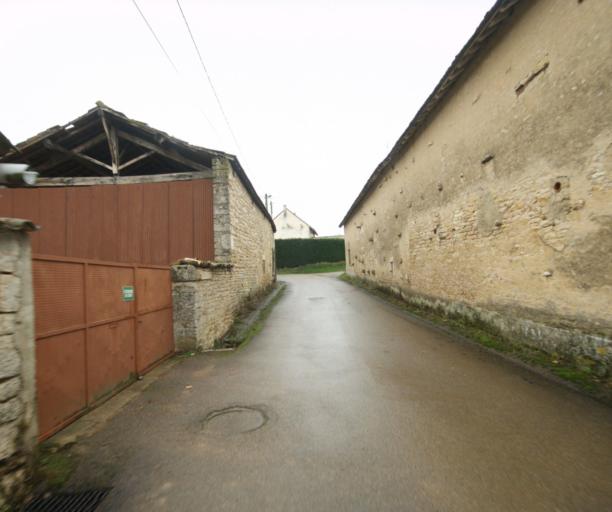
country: FR
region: Rhone-Alpes
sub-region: Departement de l'Ain
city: Pont-de-Vaux
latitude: 46.4821
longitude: 4.8670
